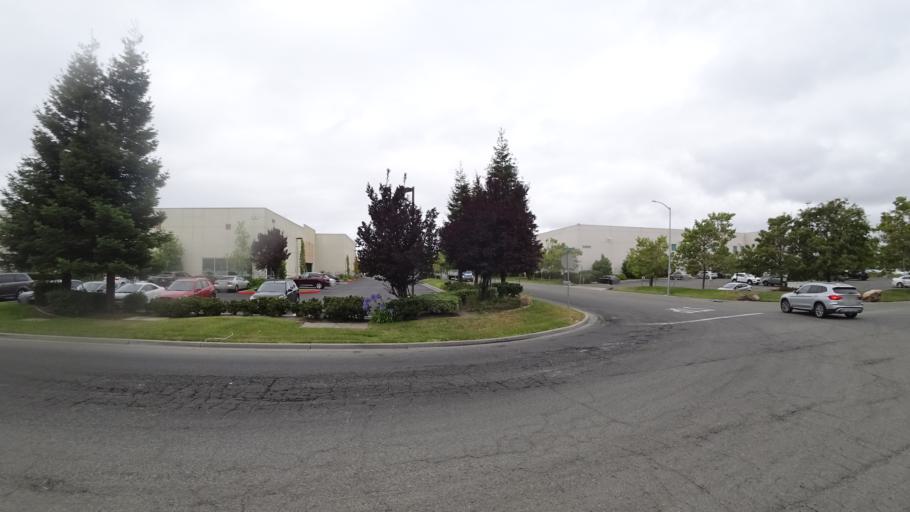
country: US
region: California
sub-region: Alameda County
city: Union City
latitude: 37.6136
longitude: -122.0613
